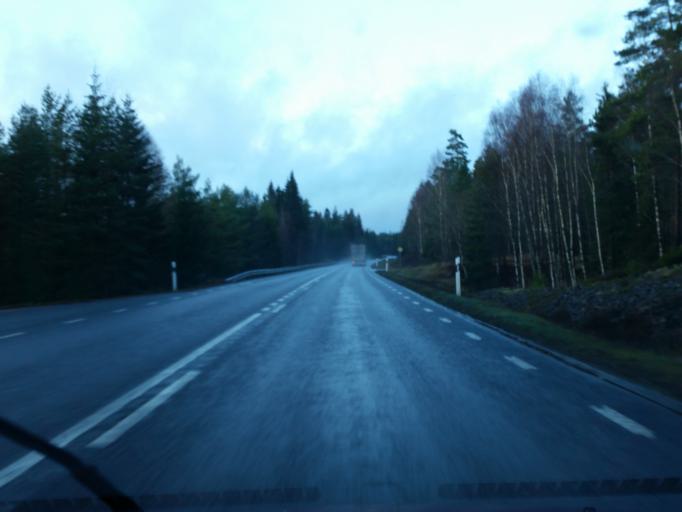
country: SE
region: Joenkoeping
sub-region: Gislaveds Kommun
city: Gislaved
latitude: 57.3319
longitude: 13.5231
